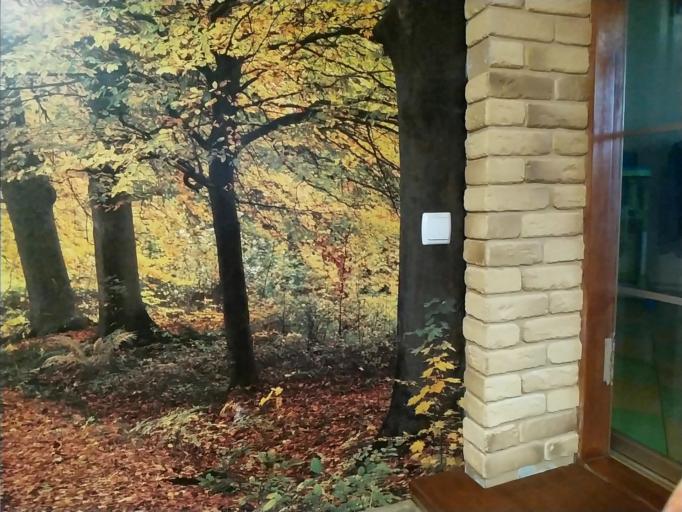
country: RU
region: Smolensk
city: Safonovo
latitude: 55.1937
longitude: 33.1271
